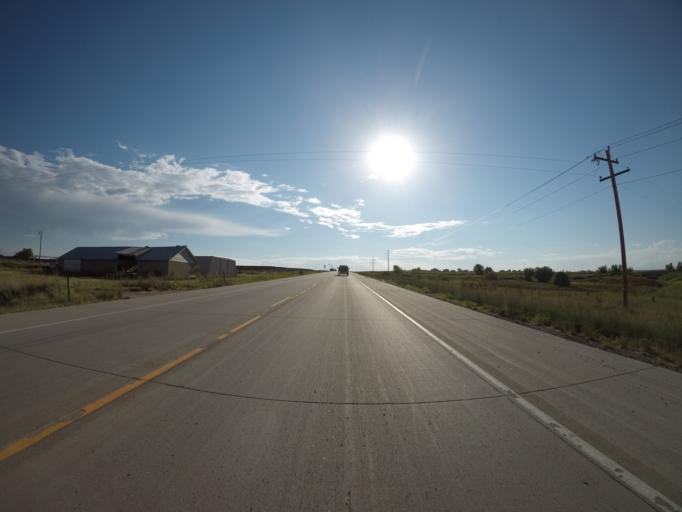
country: US
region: Colorado
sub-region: Weld County
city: Severance
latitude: 40.5816
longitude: -104.8911
